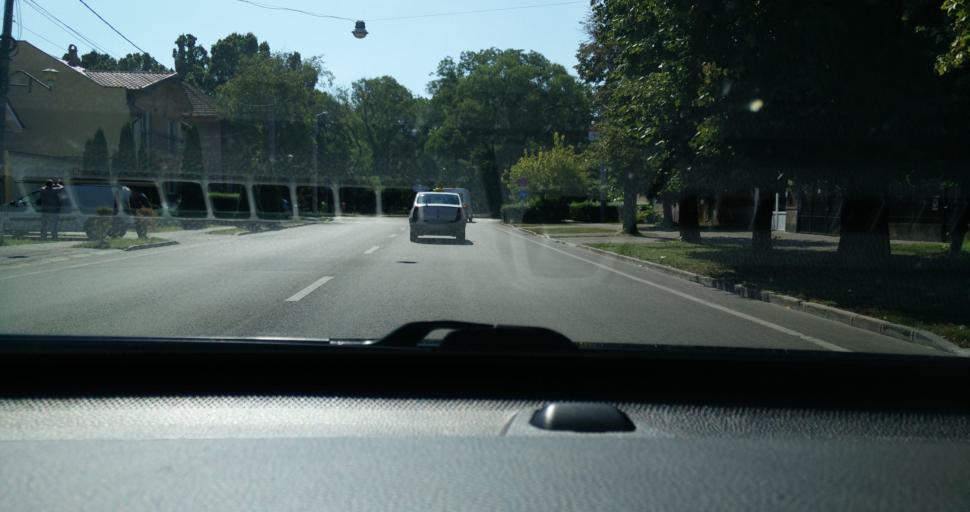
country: RO
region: Bihor
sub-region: Comuna Biharea
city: Oradea
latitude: 47.0449
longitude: 21.9334
